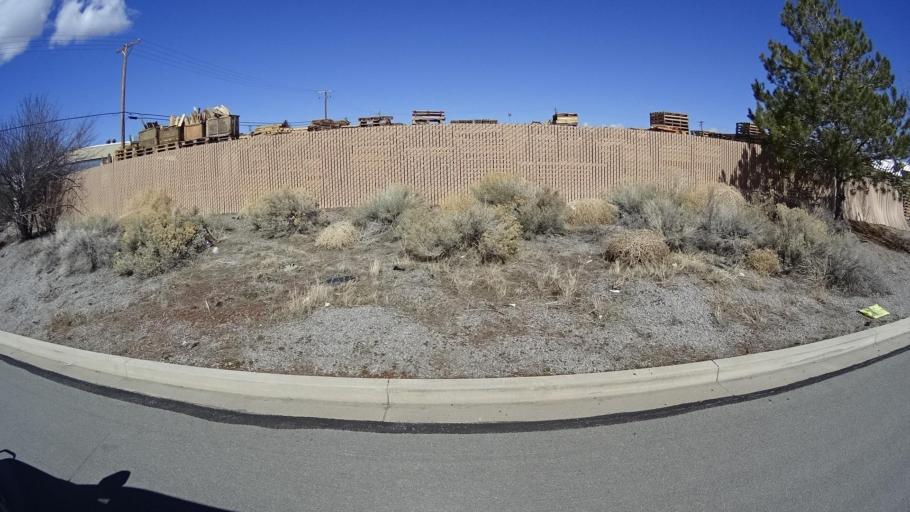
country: US
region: Nevada
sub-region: Washoe County
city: Lemmon Valley
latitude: 39.6582
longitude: -119.8843
